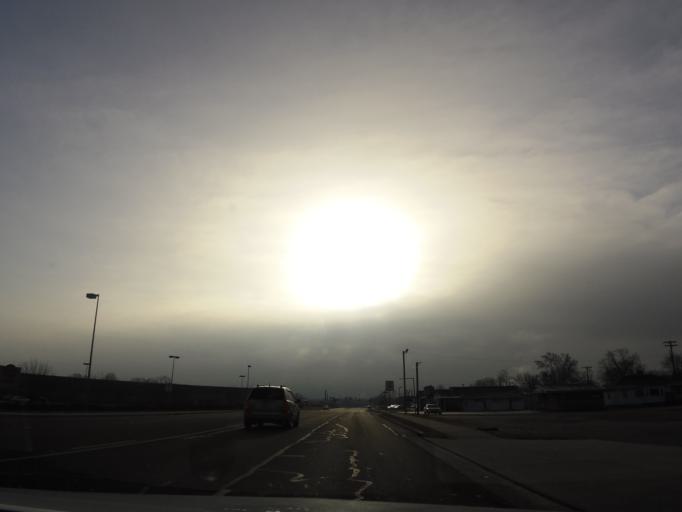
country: US
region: Indiana
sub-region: Bartholomew County
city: Columbus
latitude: 39.2196
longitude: -85.8872
